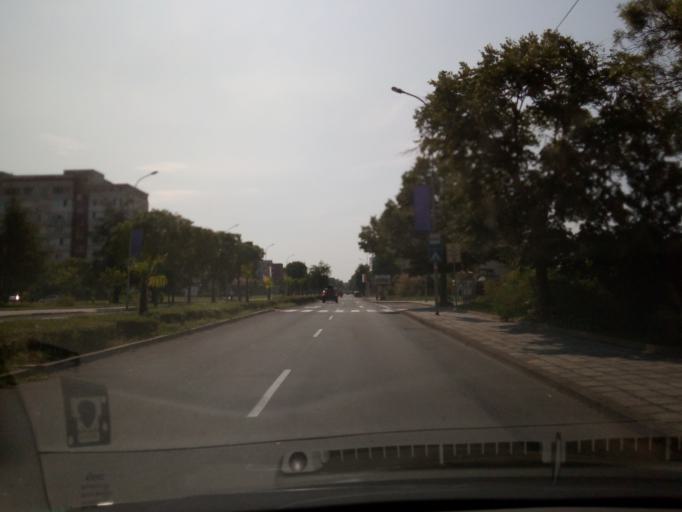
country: BG
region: Burgas
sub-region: Obshtina Pomorie
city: Pomorie
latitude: 42.5625
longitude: 27.6303
